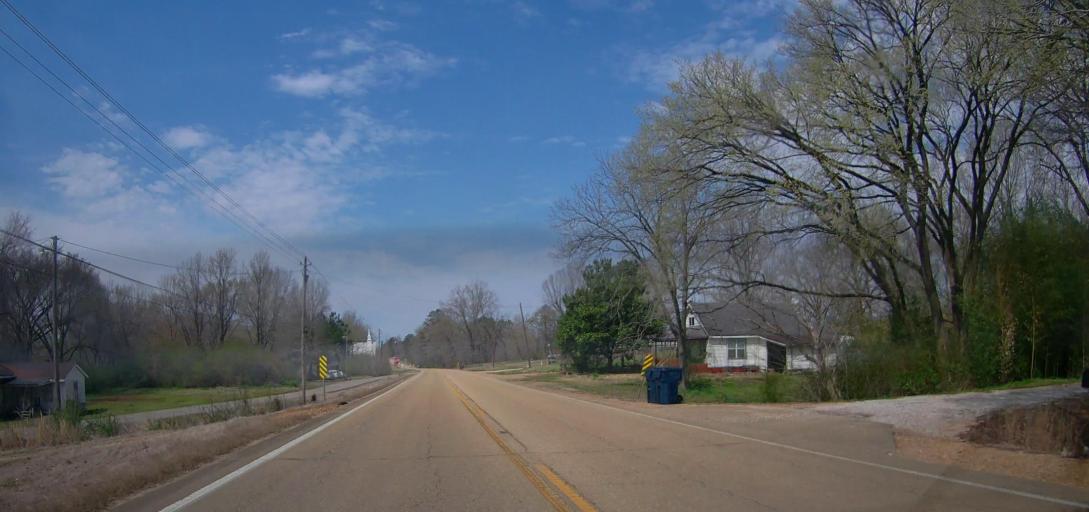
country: US
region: Mississippi
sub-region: Marshall County
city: Holly Springs
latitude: 34.6310
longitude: -89.2727
